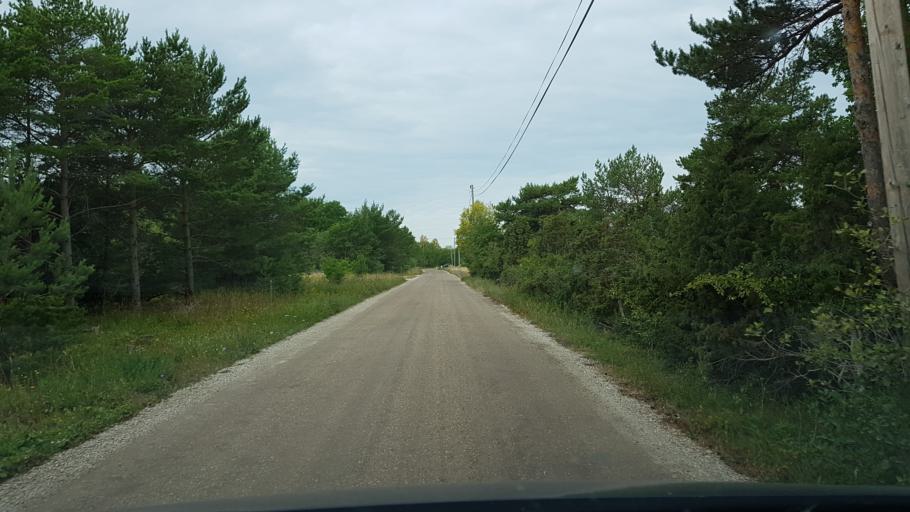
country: SE
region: Gotland
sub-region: Gotland
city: Visby
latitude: 57.8029
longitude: 18.5040
